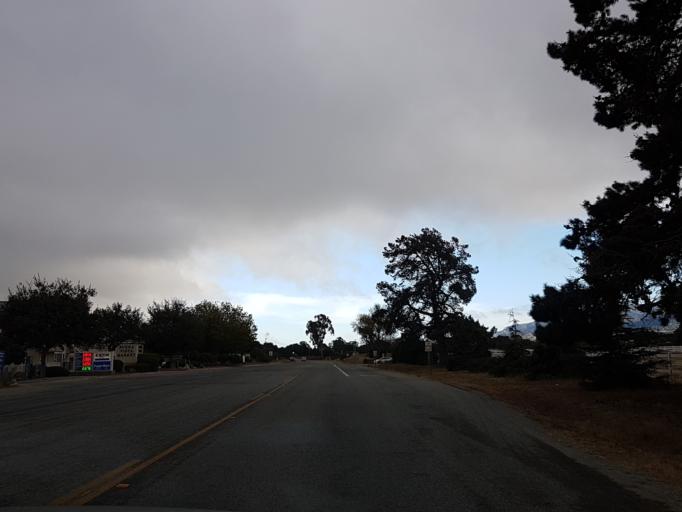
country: US
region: California
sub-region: Monterey County
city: Salinas
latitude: 36.6023
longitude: -121.6350
